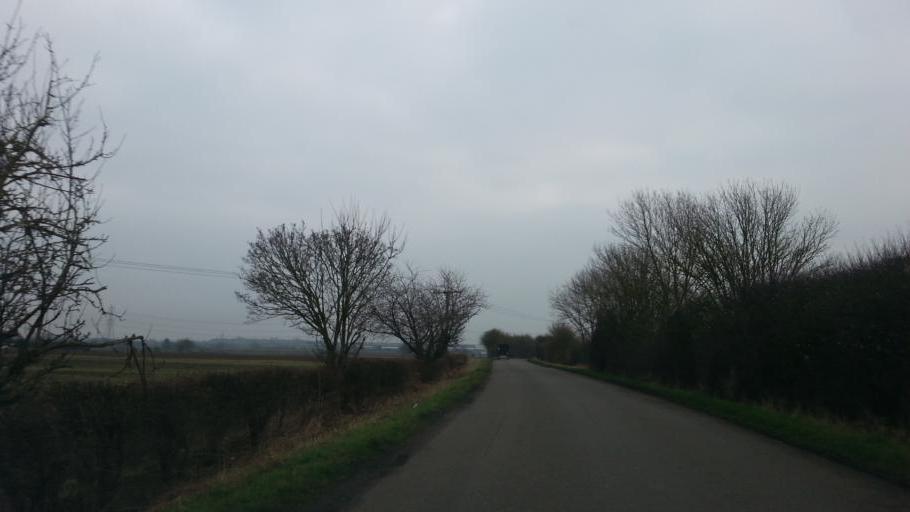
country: GB
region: England
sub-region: Lincolnshire
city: Long Bennington
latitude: 53.0022
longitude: -0.7833
